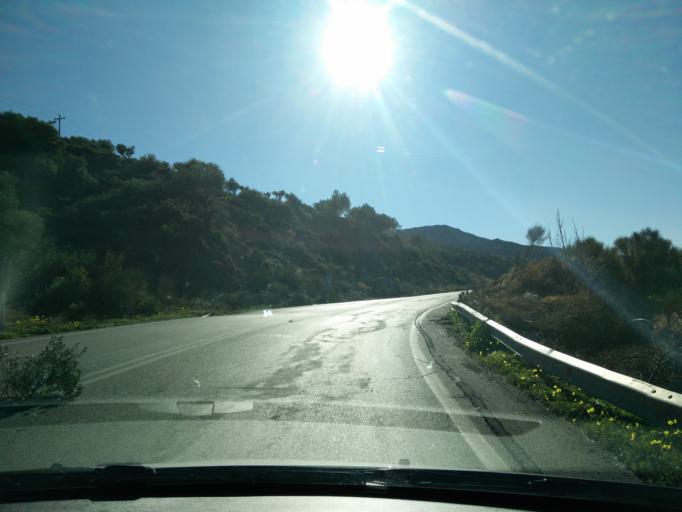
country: GR
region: Crete
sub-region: Nomos Irakleiou
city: Arkalochori
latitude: 35.0738
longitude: 25.3609
